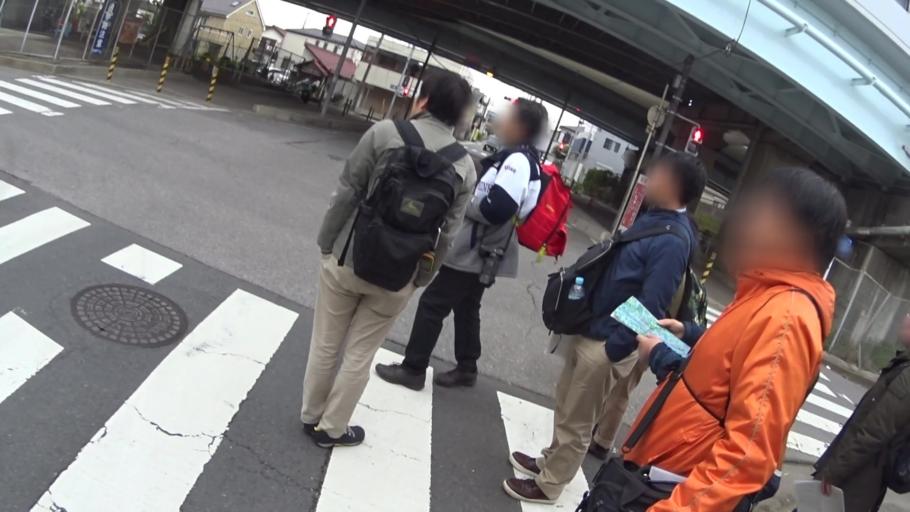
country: JP
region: Saitama
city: Yashio-shi
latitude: 35.8261
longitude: 139.8528
